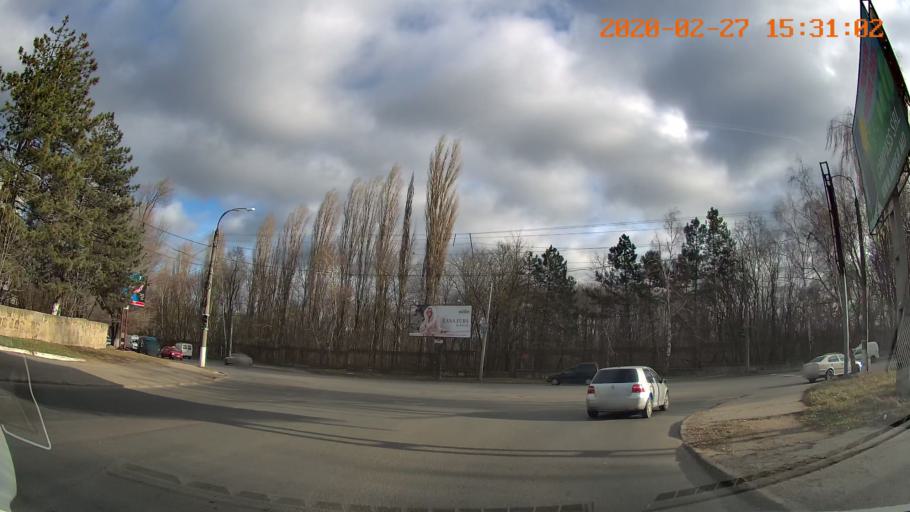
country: MD
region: Chisinau
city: Chisinau
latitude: 46.9792
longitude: 28.8838
